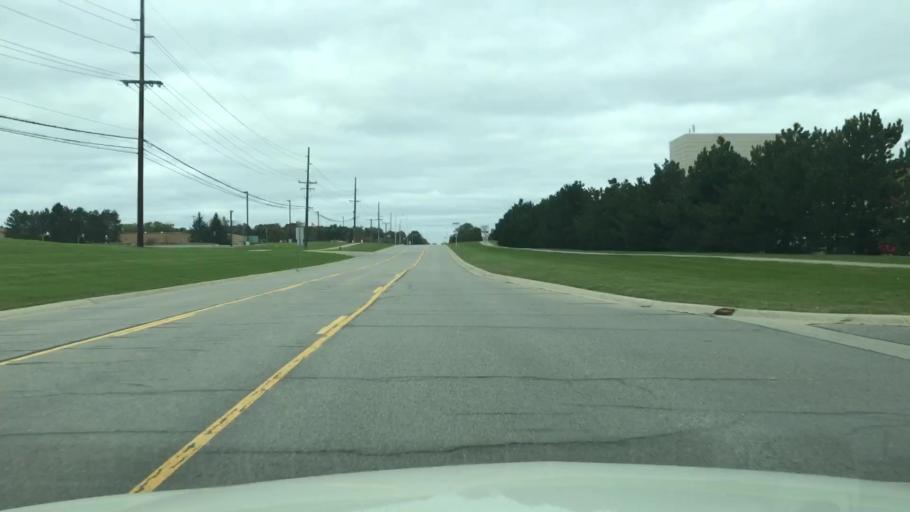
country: US
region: Michigan
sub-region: Oakland County
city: Rochester
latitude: 42.6975
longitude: -83.1234
